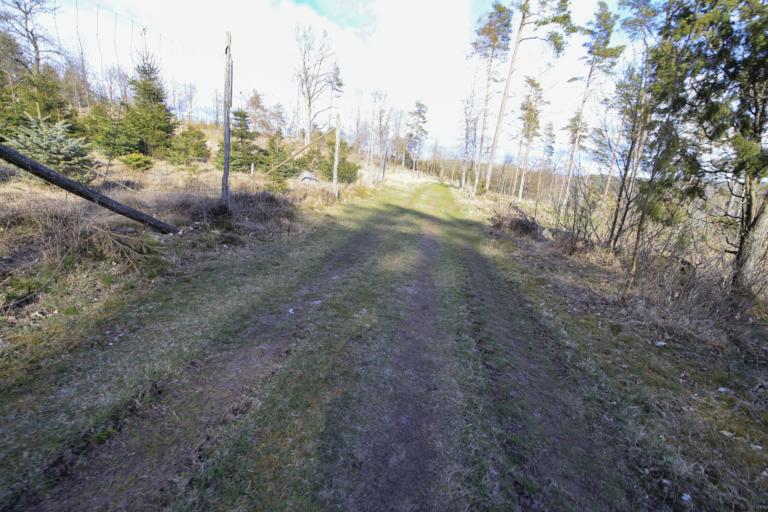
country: SE
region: Halland
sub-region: Varbergs Kommun
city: Varberg
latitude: 57.1725
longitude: 12.2700
